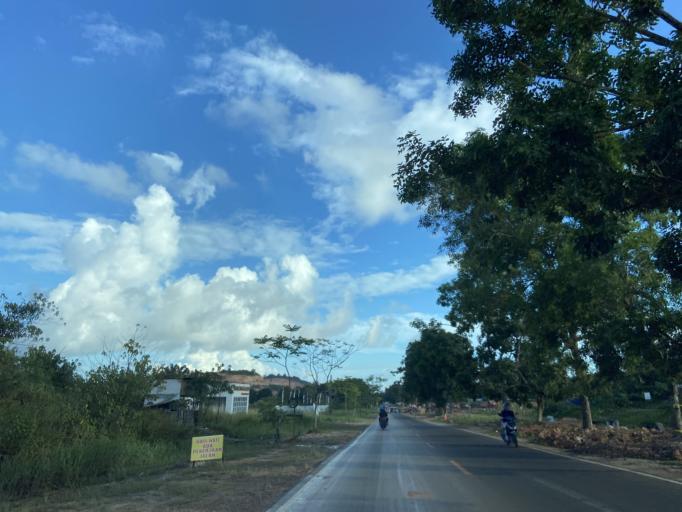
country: SG
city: Singapore
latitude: 1.0219
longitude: 104.0124
